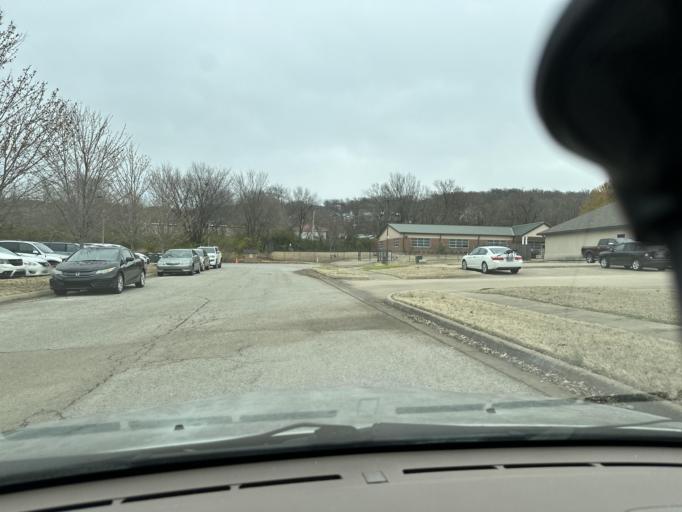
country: US
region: Arkansas
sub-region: Washington County
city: Fayetteville
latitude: 36.0936
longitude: -94.1554
